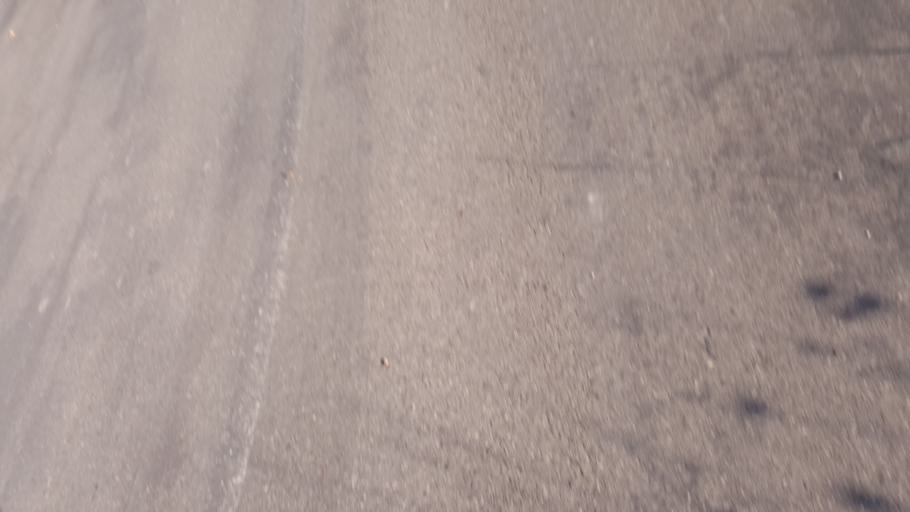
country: IT
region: Emilia-Romagna
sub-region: Provincia di Piacenza
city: Fiorenzuola d'Arda
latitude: 44.9526
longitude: 9.9107
